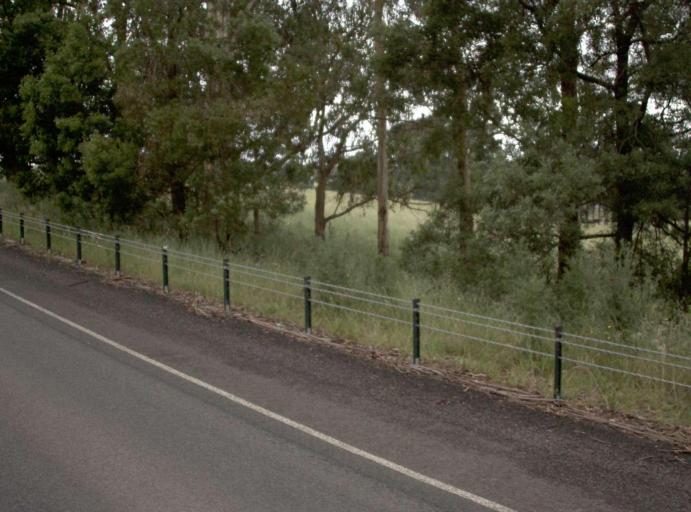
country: AU
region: Victoria
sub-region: Baw Baw
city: Warragul
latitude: -38.0781
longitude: 145.9665
